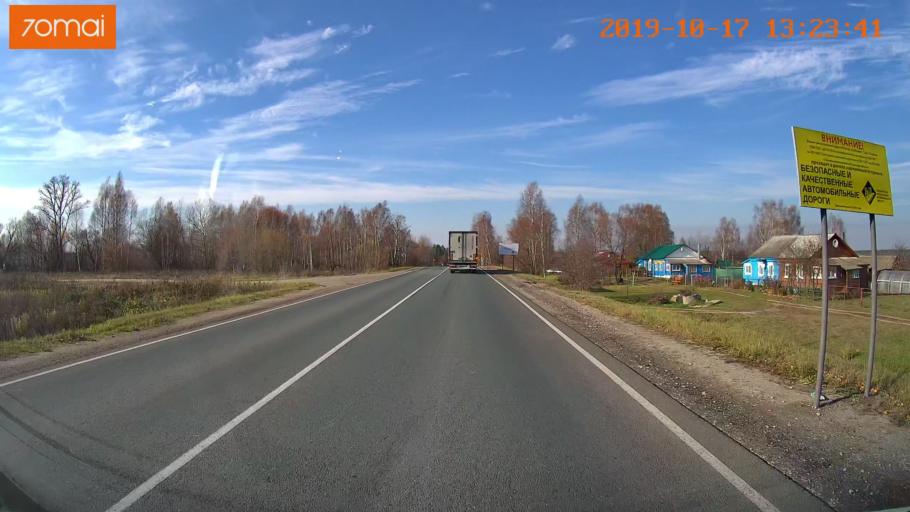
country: RU
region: Rjazan
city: Gus'-Zheleznyy
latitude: 55.0908
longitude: 40.9757
